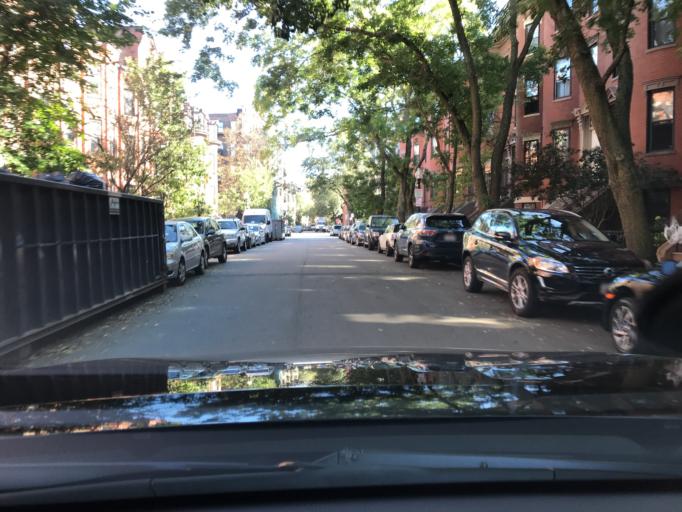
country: US
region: Massachusetts
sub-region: Suffolk County
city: Boston
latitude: 42.3424
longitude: -71.0815
